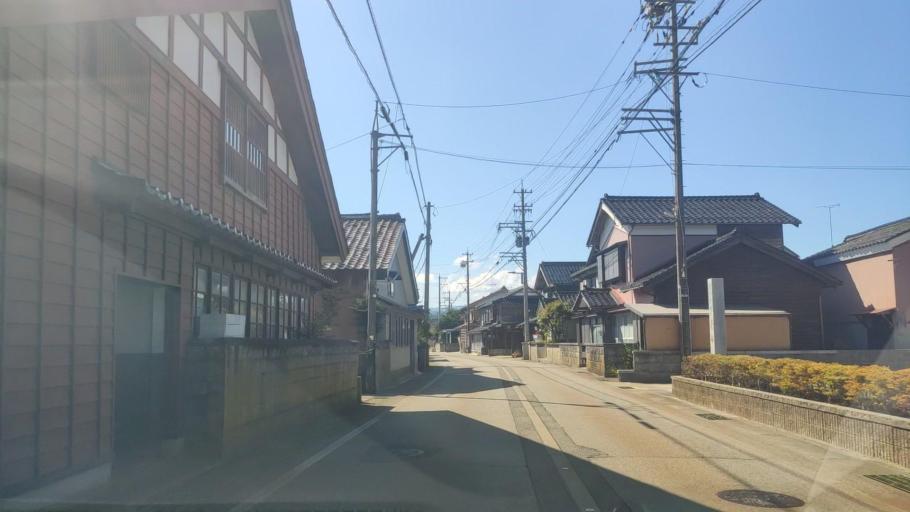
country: JP
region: Ishikawa
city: Nanao
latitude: 37.4416
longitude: 137.2778
